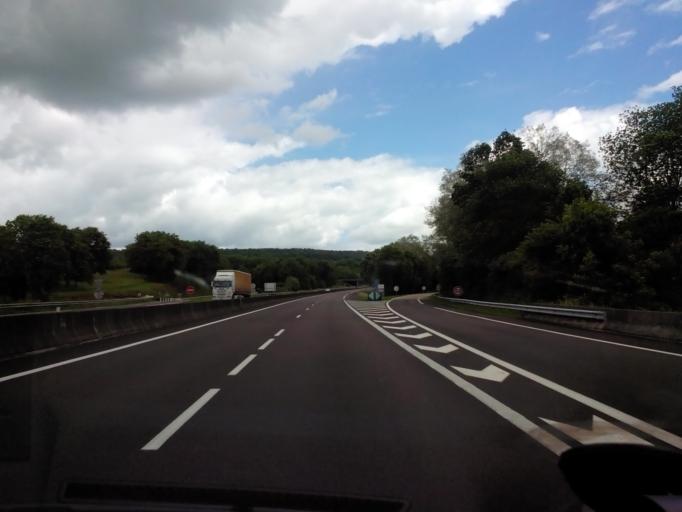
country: FR
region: Champagne-Ardenne
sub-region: Departement de la Haute-Marne
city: Rolampont
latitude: 47.9419
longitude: 5.2993
